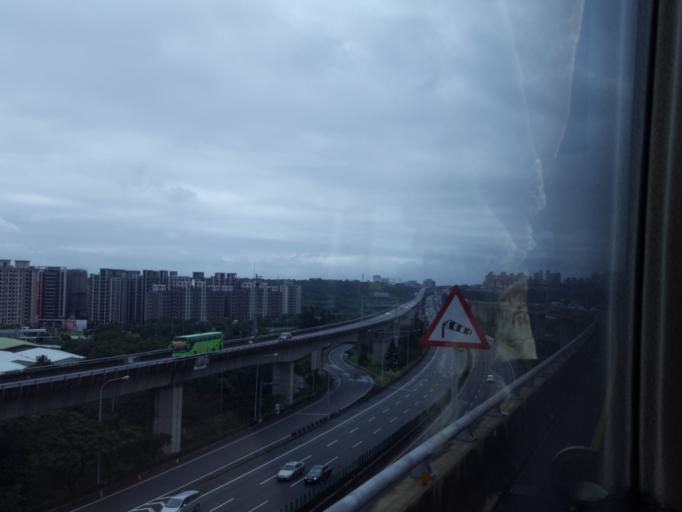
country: TW
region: Taiwan
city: Daxi
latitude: 24.9058
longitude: 121.1631
